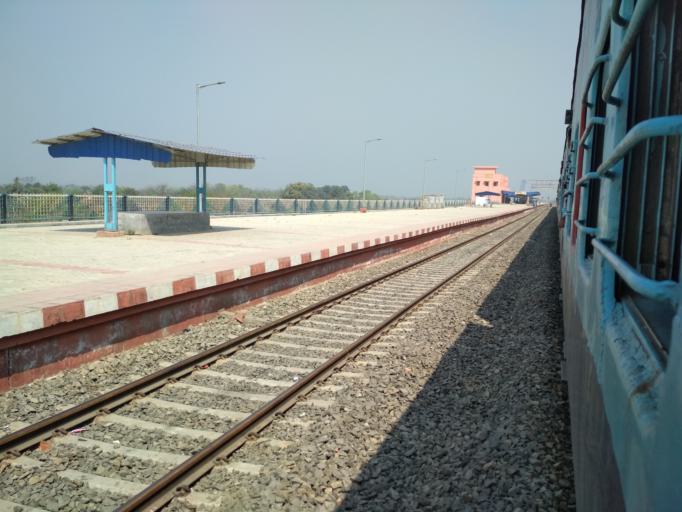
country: IN
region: Bihar
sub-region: Munger
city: Munger
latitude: 25.4259
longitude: 86.4386
